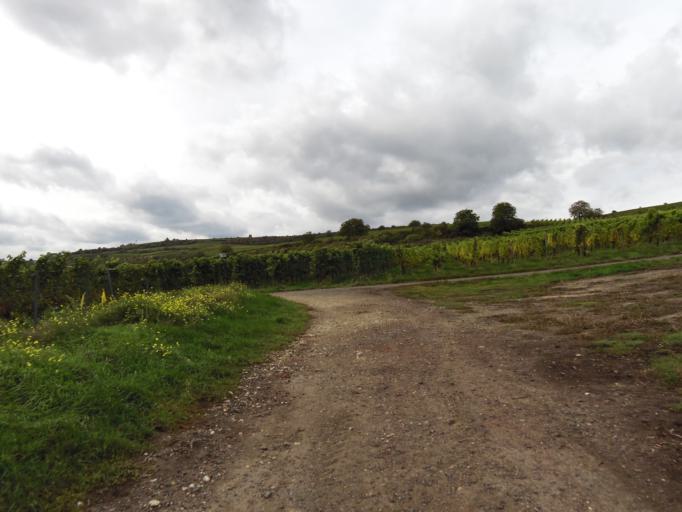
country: DE
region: Rheinland-Pfalz
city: Grunstadt
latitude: 49.5556
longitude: 8.1536
